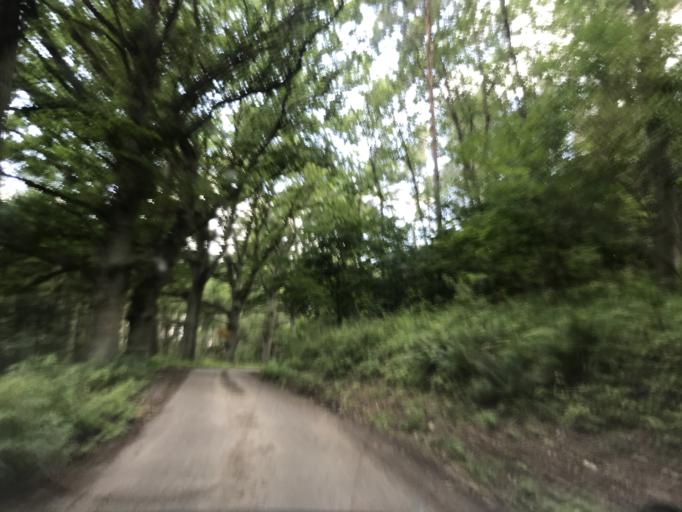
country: PL
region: West Pomeranian Voivodeship
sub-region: Powiat stargardzki
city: Insko
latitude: 53.4849
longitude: 15.5048
